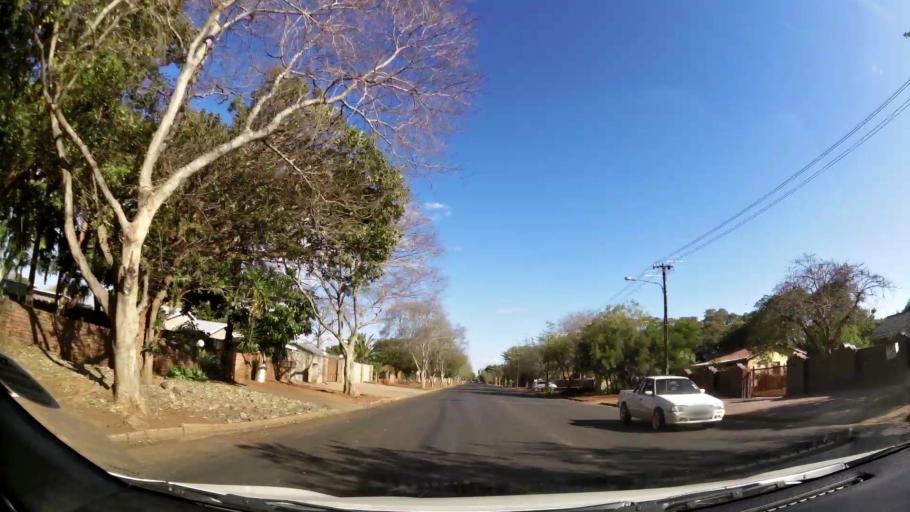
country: ZA
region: Limpopo
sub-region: Waterberg District Municipality
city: Mokopane
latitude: -24.1813
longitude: 29.0003
